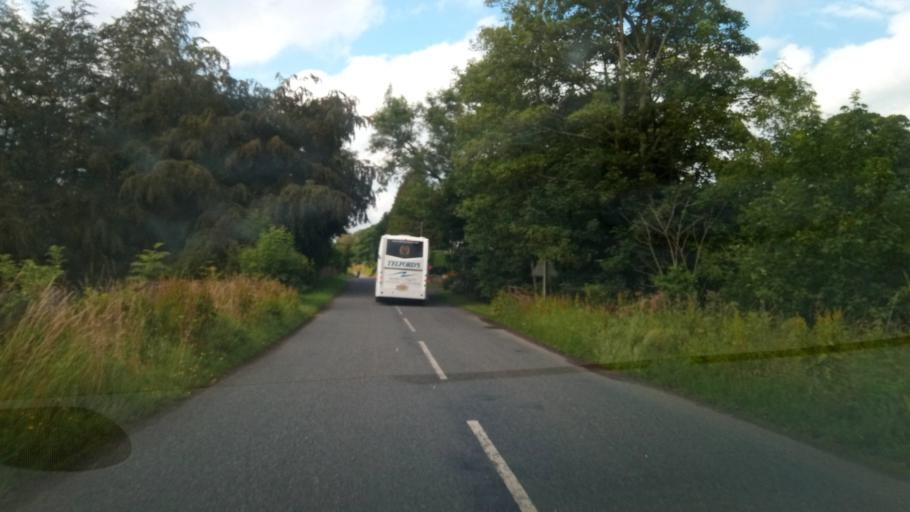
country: GB
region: Scotland
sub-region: Dumfries and Galloway
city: Langholm
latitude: 55.0598
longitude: -2.9515
